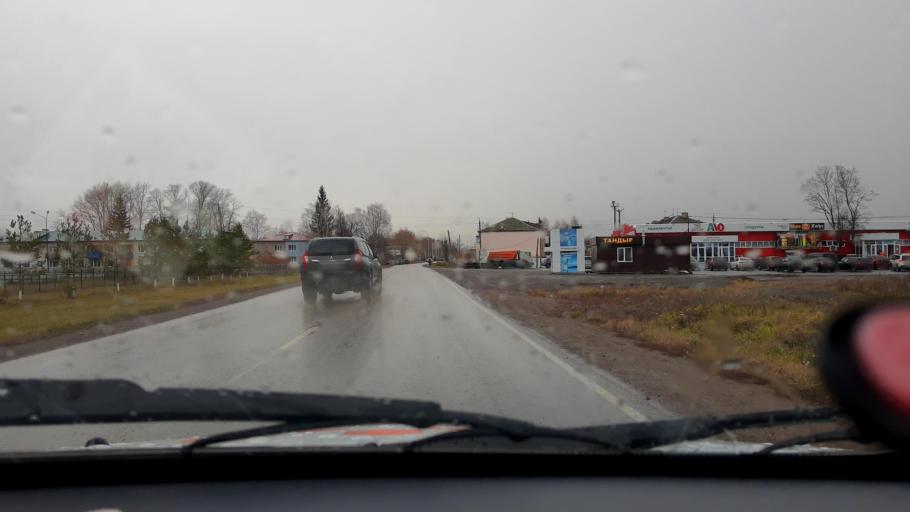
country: RU
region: Bashkortostan
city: Mikhaylovka
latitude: 54.8104
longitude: 55.8134
